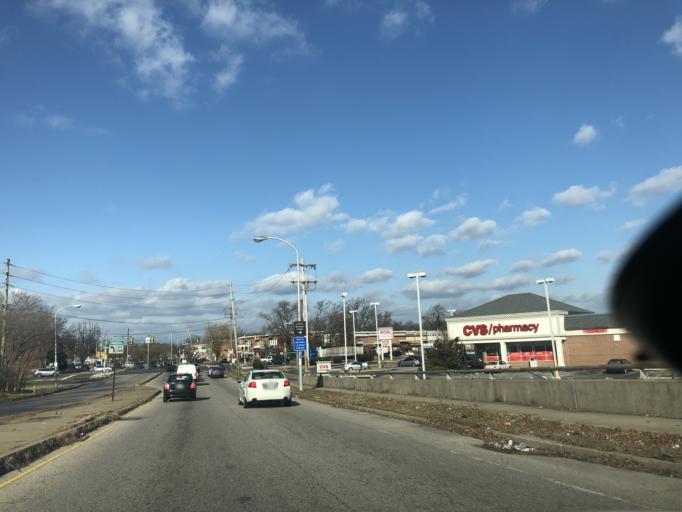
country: US
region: Pennsylvania
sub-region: Delaware County
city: Colwyn
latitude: 39.9100
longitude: -75.2297
